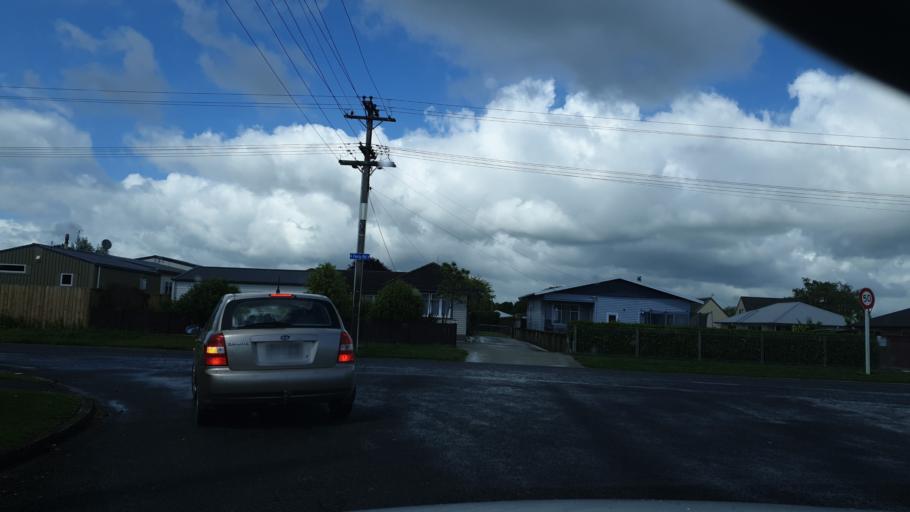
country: NZ
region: Waikato
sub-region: Matamata-Piako District
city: Matamata
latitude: -37.8064
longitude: 175.7658
